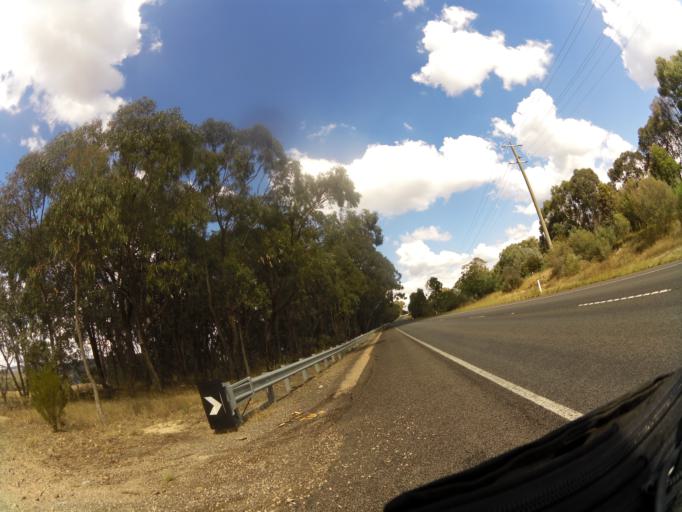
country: AU
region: Victoria
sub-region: Benalla
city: Benalla
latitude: -36.7872
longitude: 146.0105
